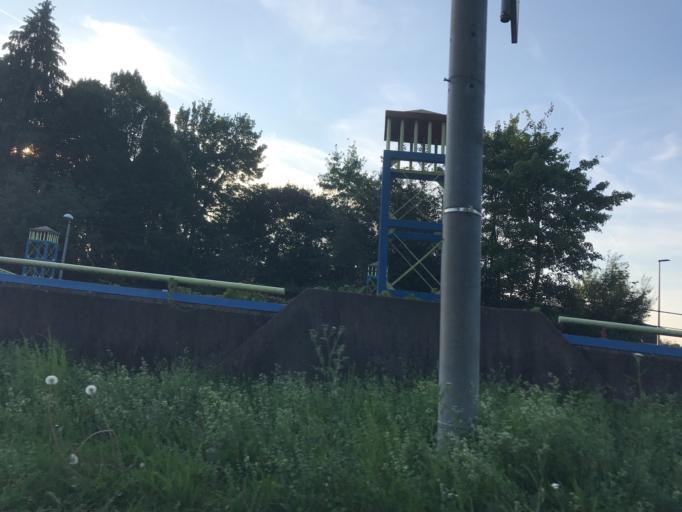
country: DE
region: Baden-Wuerttemberg
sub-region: Regierungsbezirk Stuttgart
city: Korntal
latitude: 48.8103
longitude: 9.1083
